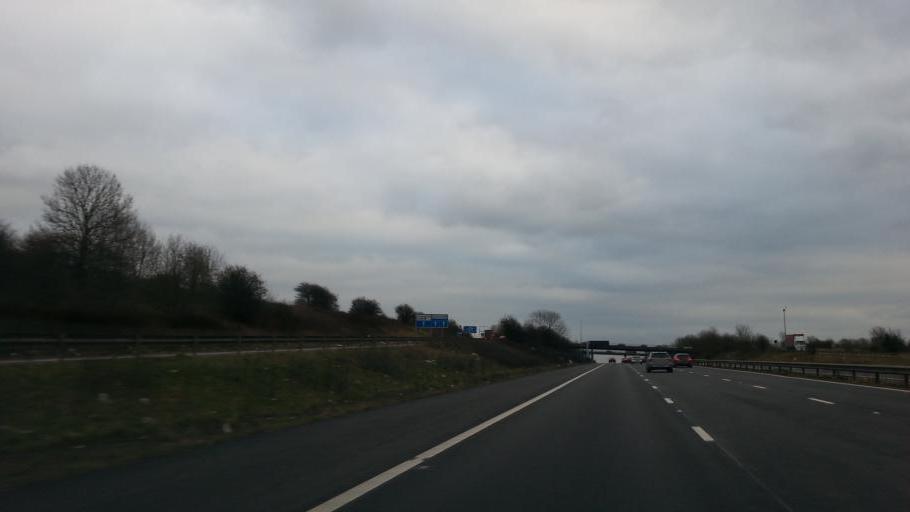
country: GB
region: England
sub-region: Warwickshire
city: Rugby
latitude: 52.4089
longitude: -1.2516
